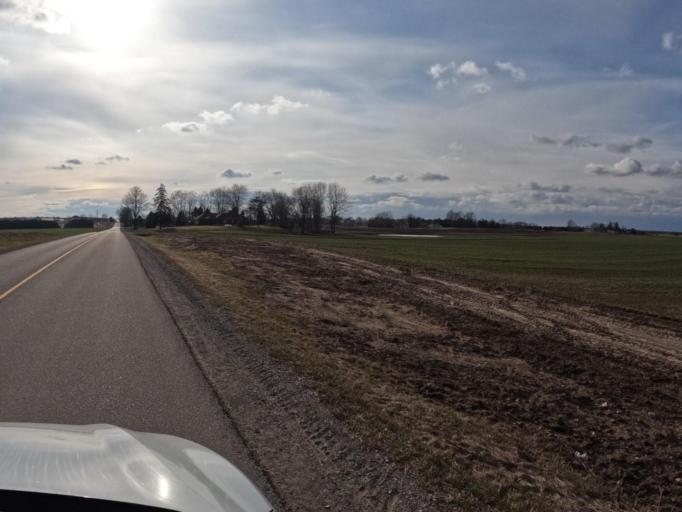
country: CA
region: Ontario
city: Brant
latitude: 43.0091
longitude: -80.3859
